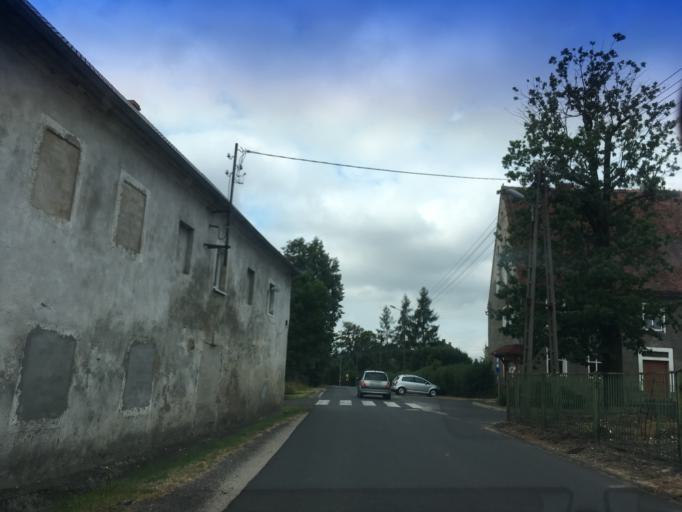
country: PL
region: Lower Silesian Voivodeship
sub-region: Powiat zgorzelecki
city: Sulikow
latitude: 51.1046
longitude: 15.0669
